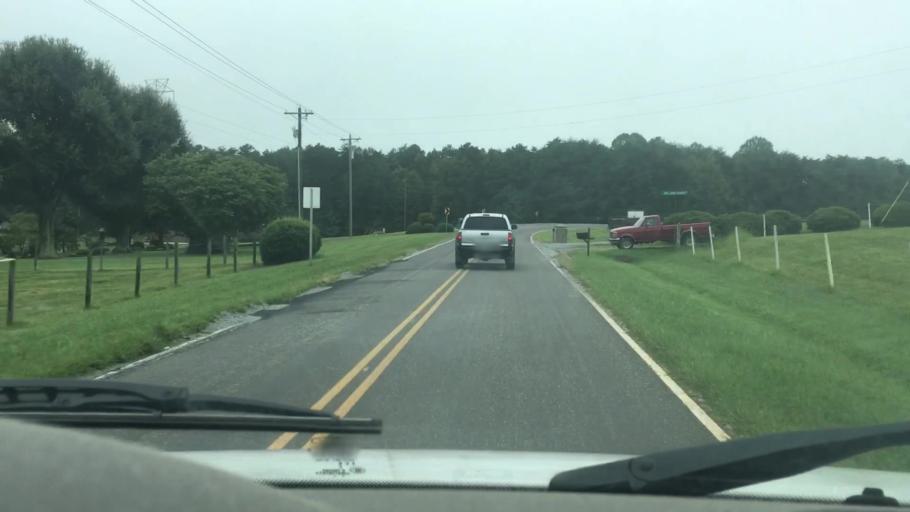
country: US
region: North Carolina
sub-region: Gaston County
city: Davidson
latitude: 35.5240
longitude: -80.7869
